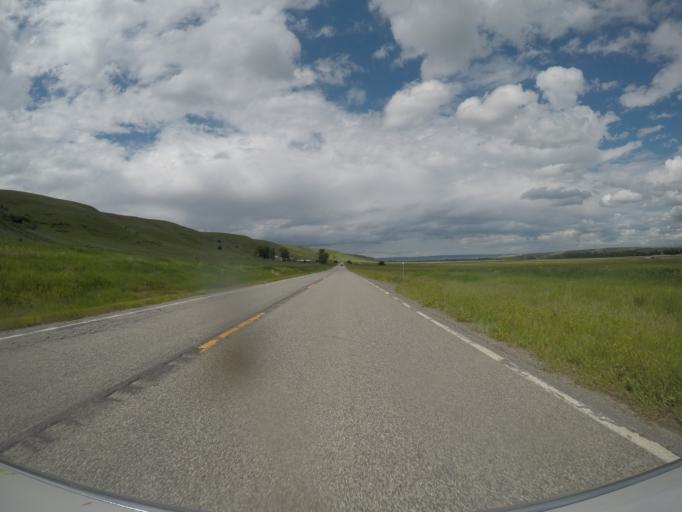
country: US
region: Montana
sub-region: Sweet Grass County
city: Big Timber
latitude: 45.7749
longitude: -109.9878
